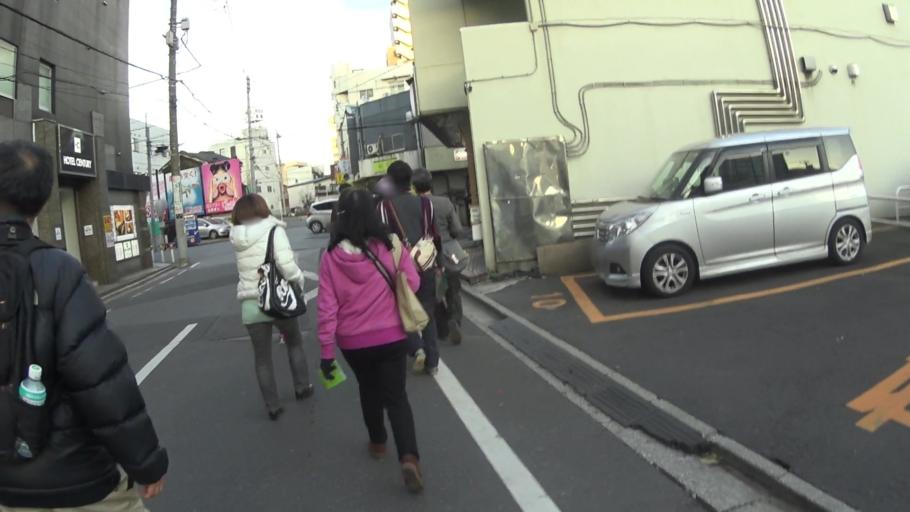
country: JP
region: Chiba
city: Chiba
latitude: 35.6134
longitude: 140.1214
